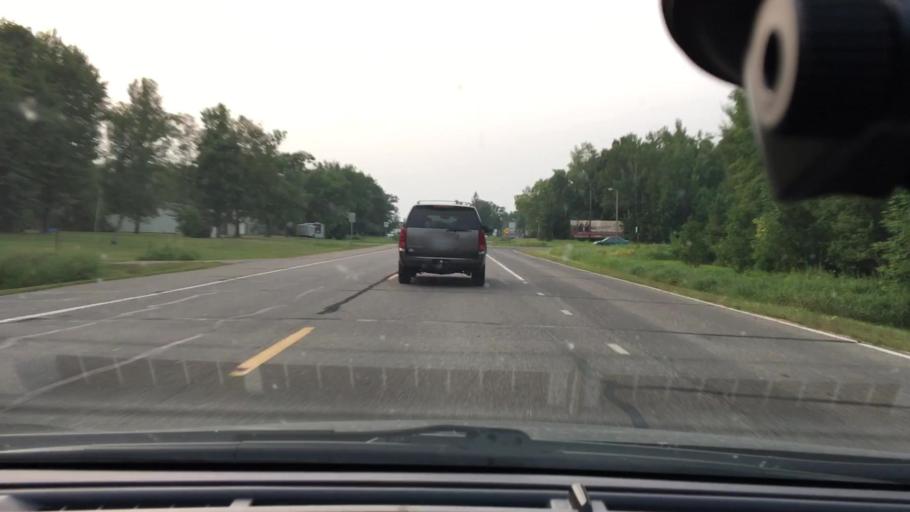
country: US
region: Minnesota
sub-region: Crow Wing County
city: Crosby
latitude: 46.4711
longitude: -93.8892
